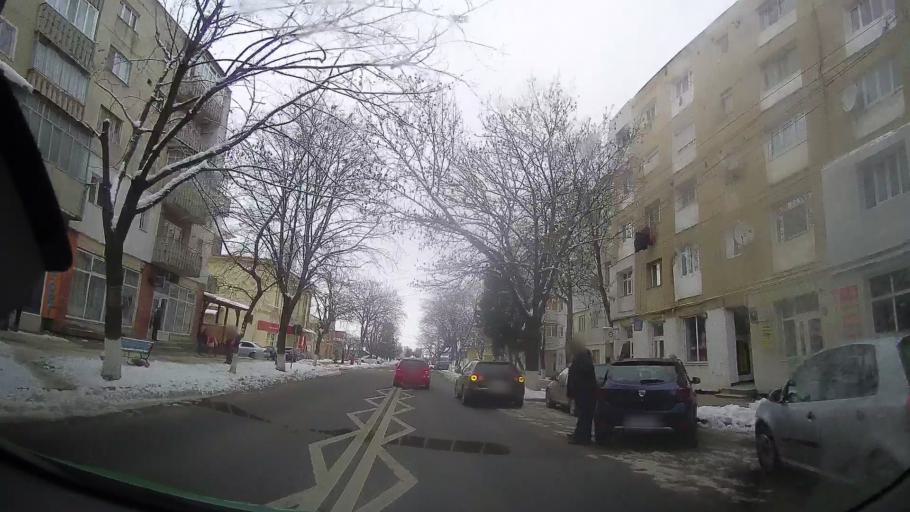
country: RO
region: Vaslui
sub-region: Comuna Negresti
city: Negresti
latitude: 46.8350
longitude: 27.4538
